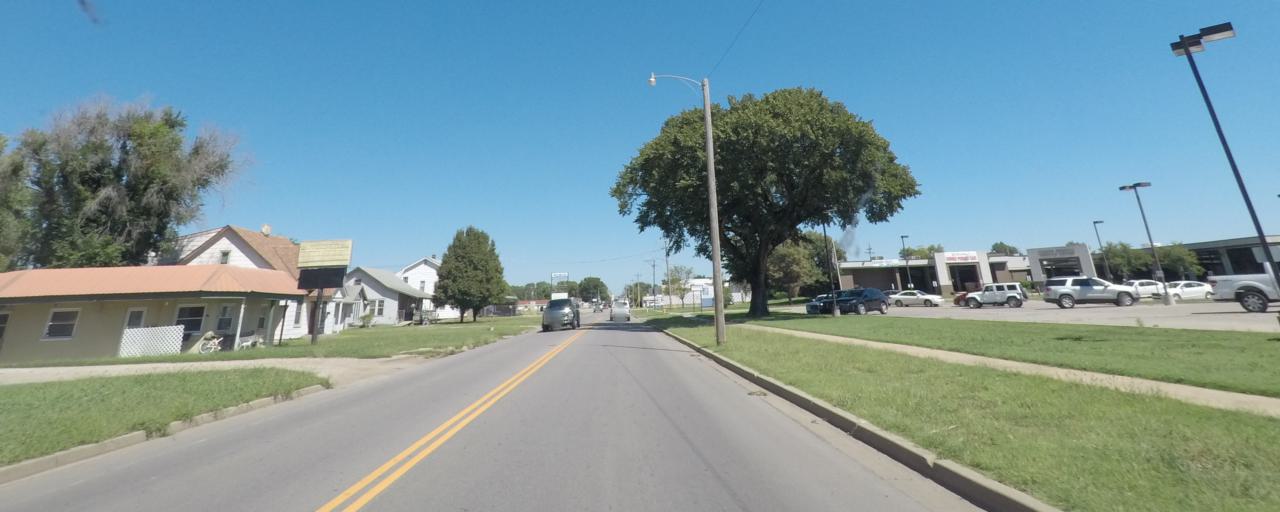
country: US
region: Kansas
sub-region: Sumner County
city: Wellington
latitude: 37.2778
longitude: -97.3942
